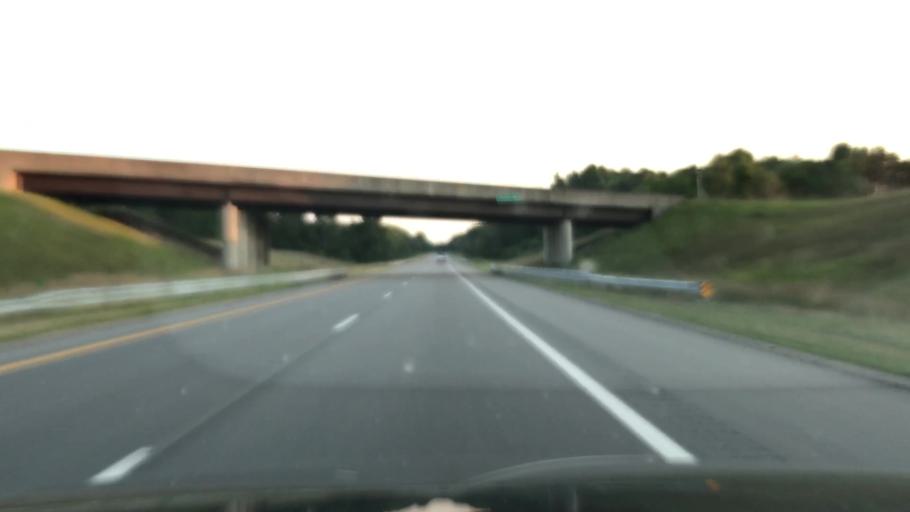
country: US
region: Michigan
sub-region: Montcalm County
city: Howard City
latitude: 43.4578
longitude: -85.4809
